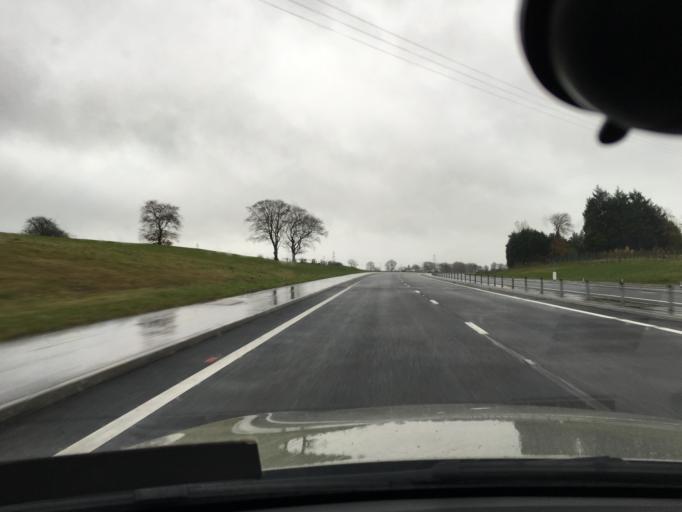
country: GB
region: Northern Ireland
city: Carnmoney
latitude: 54.7373
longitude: -5.9624
